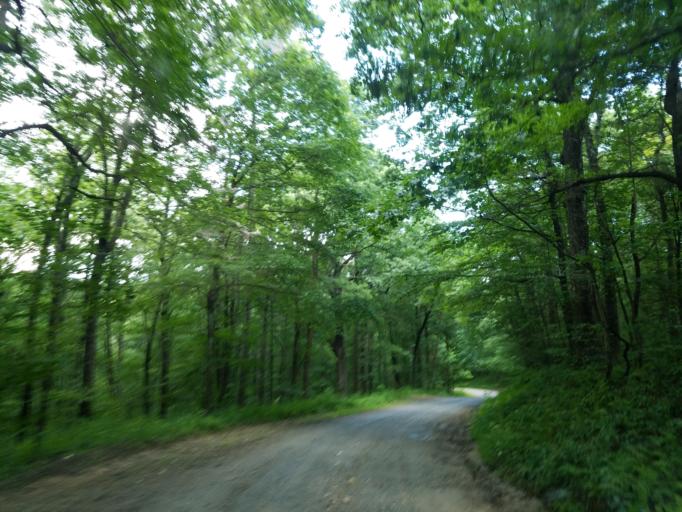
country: US
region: Georgia
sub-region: Lumpkin County
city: Dahlonega
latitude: 34.6356
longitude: -84.1752
